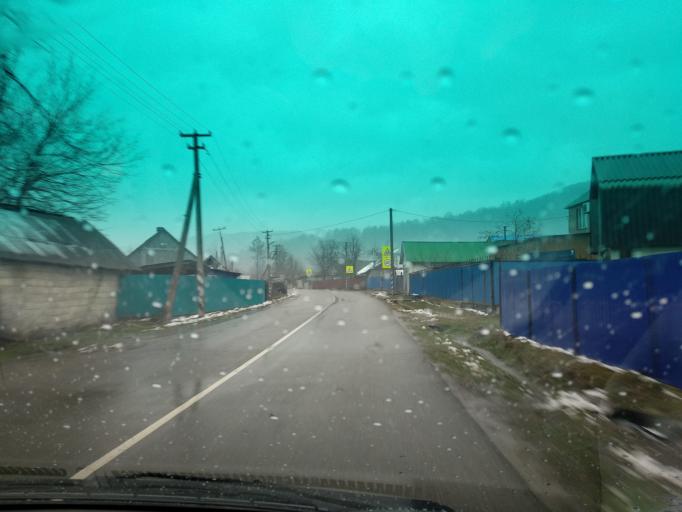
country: RU
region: Krasnodarskiy
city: Khadyzhensk
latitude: 44.2463
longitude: 39.3757
